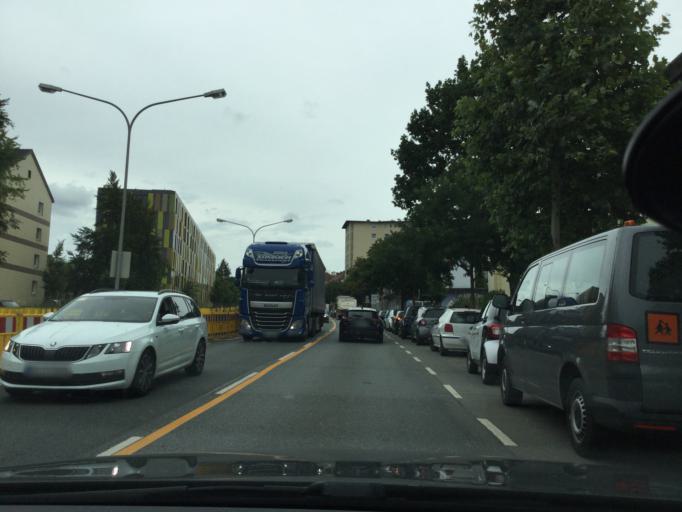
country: DE
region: Bavaria
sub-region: Upper Franconia
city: Hof
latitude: 50.3155
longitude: 11.9058
